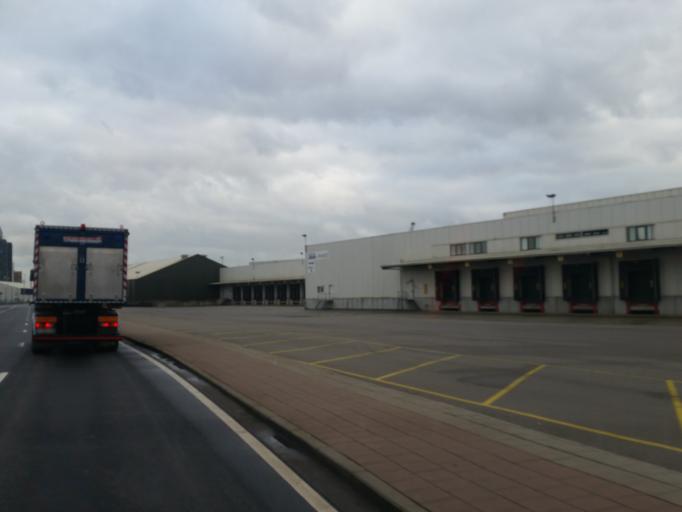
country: BE
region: Flanders
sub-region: Provincie Antwerpen
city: Antwerpen
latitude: 51.2639
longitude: 4.3896
